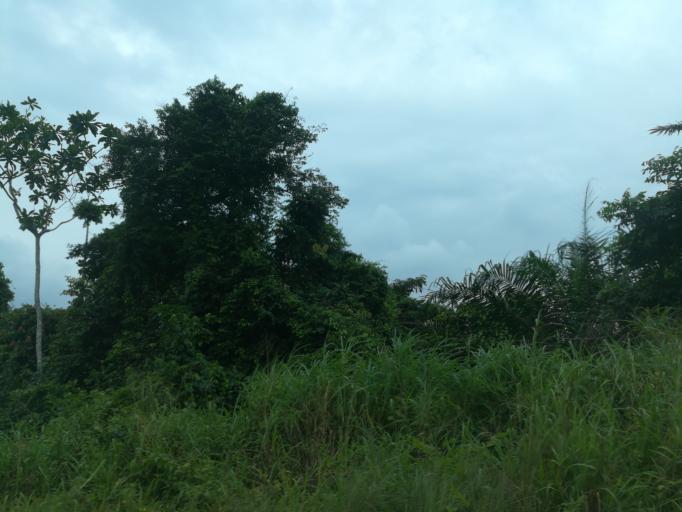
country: NG
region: Lagos
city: Ejirin
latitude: 6.6482
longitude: 3.7820
